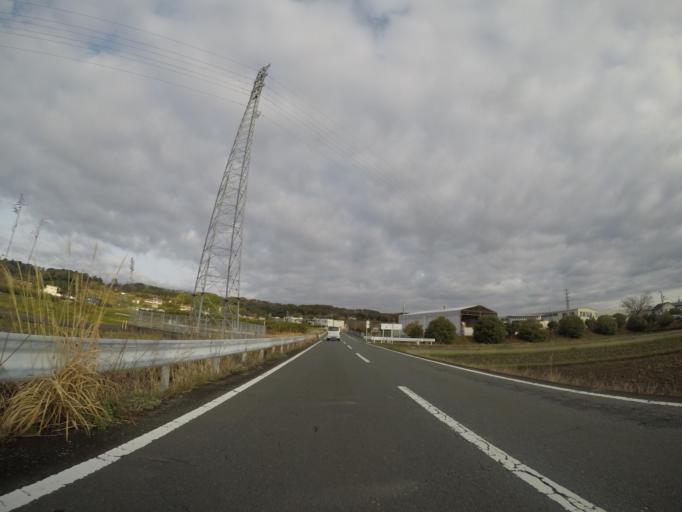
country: JP
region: Shizuoka
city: Hamakita
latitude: 34.8201
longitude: 137.7631
